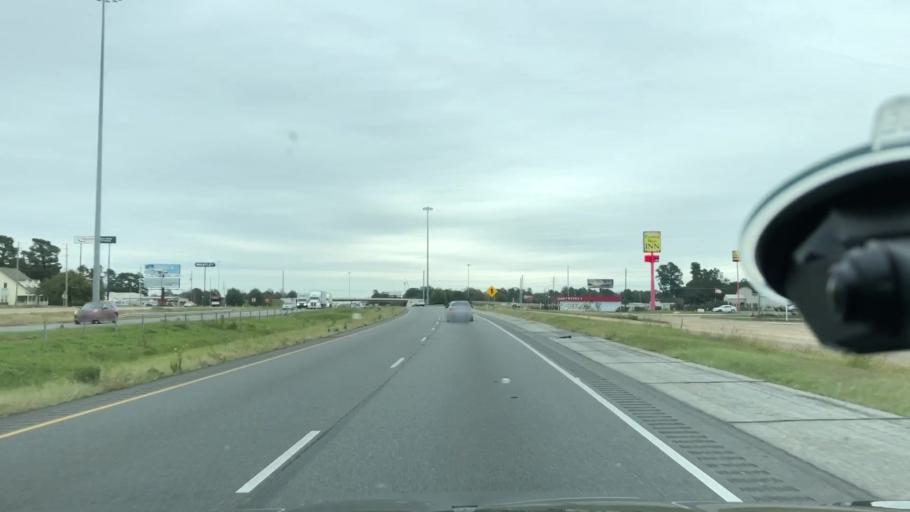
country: US
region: Arkansas
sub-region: Miller County
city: Texarkana
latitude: 33.4702
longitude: -94.0352
